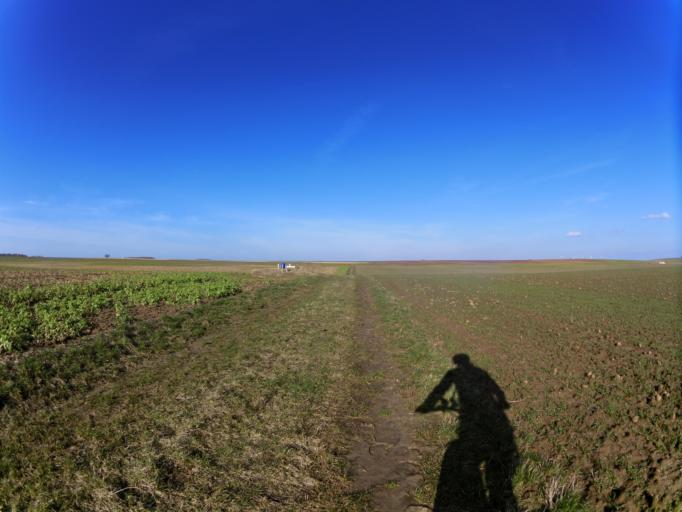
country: DE
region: Bavaria
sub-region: Regierungsbezirk Unterfranken
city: Giebelstadt
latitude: 49.6789
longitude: 9.9679
